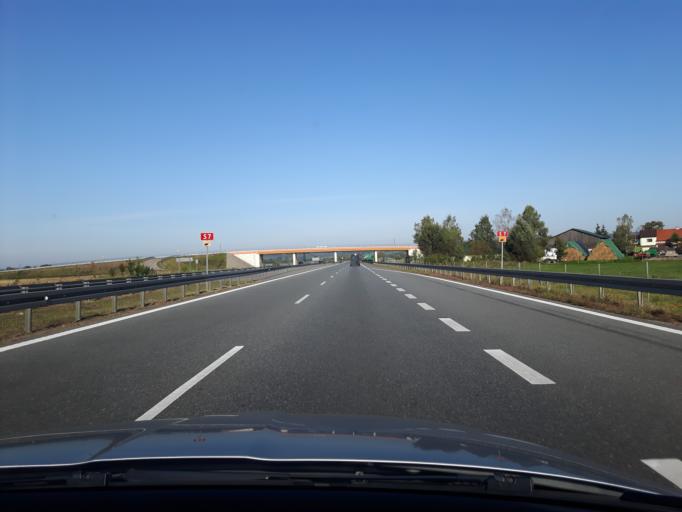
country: PL
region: Warmian-Masurian Voivodeship
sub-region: Powiat elblaski
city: Paslek
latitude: 54.0847
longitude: 19.6027
